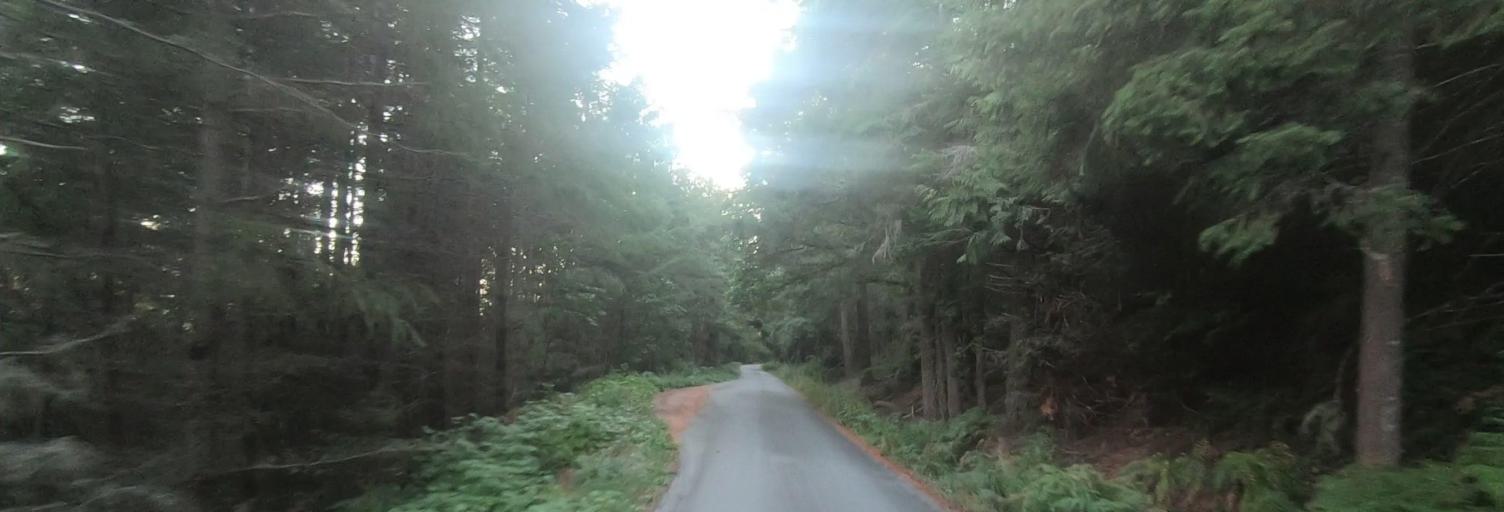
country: US
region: Washington
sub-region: Whatcom County
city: Peaceful Valley
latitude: 48.9060
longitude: -121.9612
